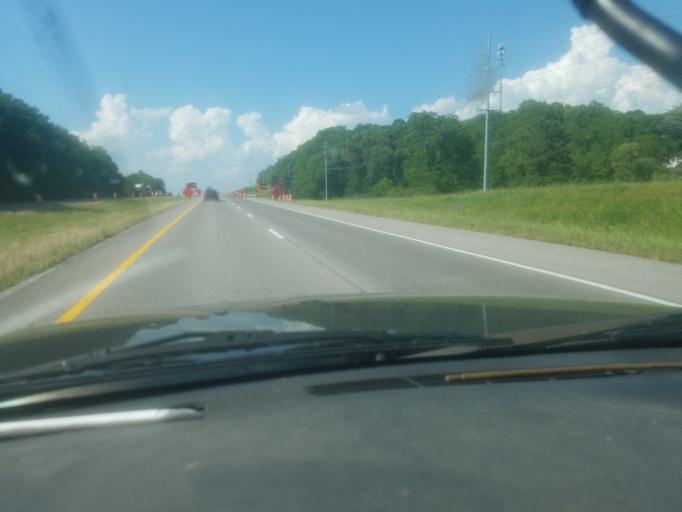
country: US
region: Tennessee
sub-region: Maury County
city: Mount Pleasant
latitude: 35.5340
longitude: -87.2216
